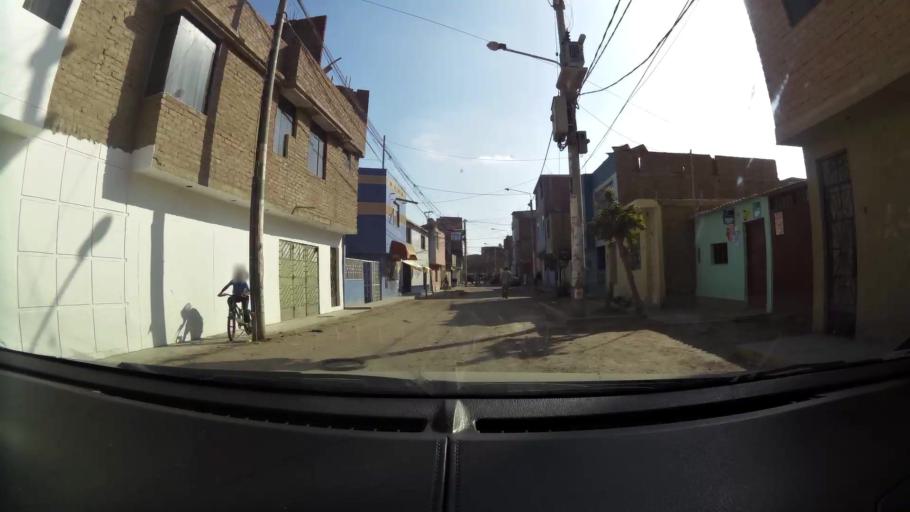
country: PE
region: Lambayeque
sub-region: Provincia de Chiclayo
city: Chiclayo
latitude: -6.7637
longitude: -79.8482
